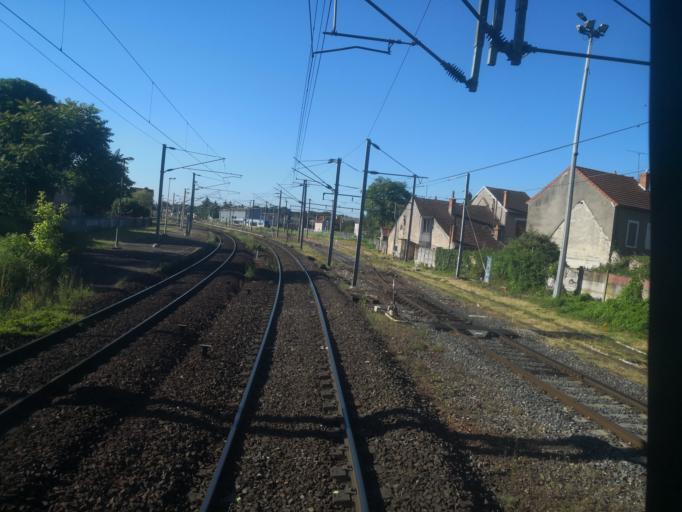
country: FR
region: Bourgogne
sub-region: Departement de la Nievre
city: Cosne-Cours-sur-Loire
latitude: 47.4127
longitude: 2.9327
